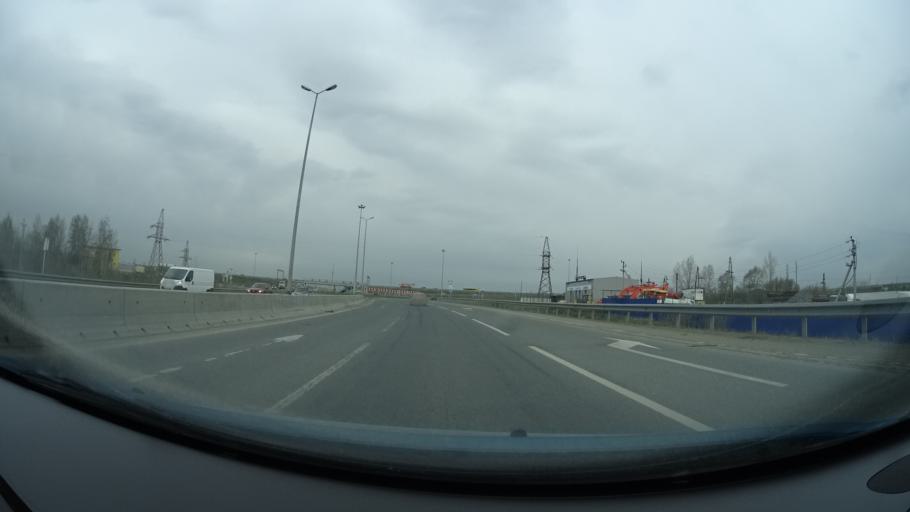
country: RU
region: Perm
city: Kondratovo
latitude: 58.0097
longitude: 56.0575
